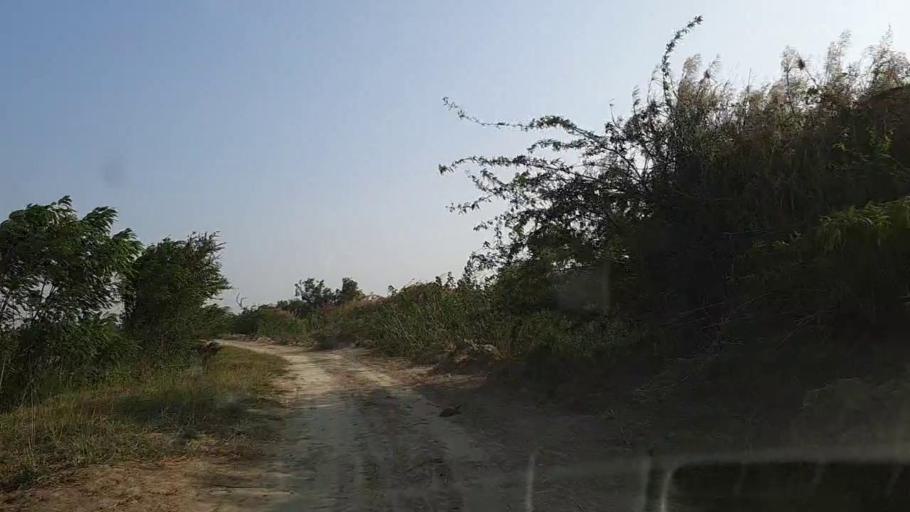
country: PK
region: Sindh
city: Mirpur Sakro
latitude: 24.5899
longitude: 67.6468
